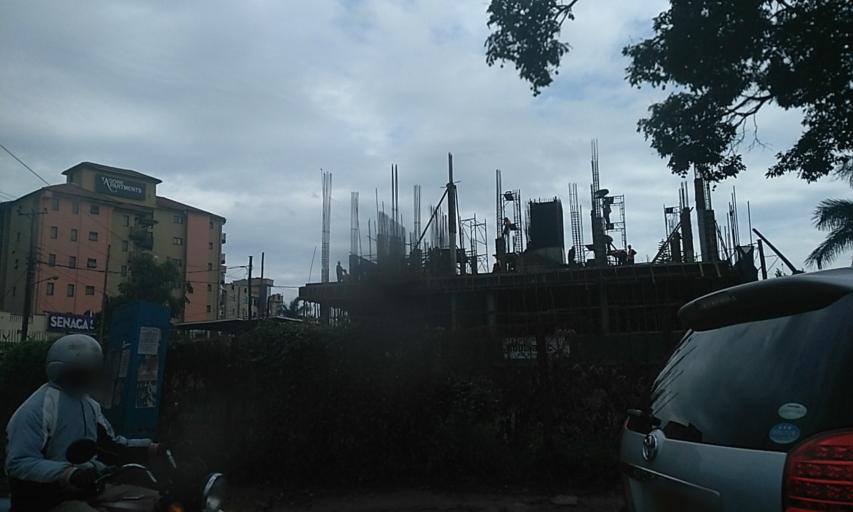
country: UG
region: Central Region
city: Kampala Central Division
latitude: 0.3387
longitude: 32.5855
